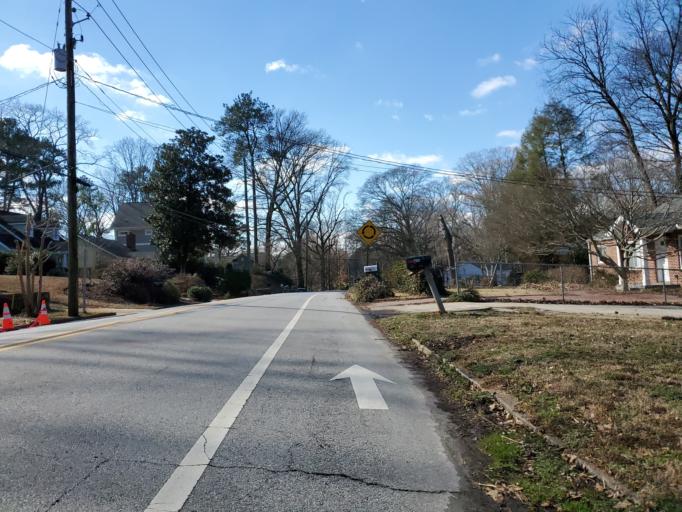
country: US
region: Georgia
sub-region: Fulton County
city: Atlanta
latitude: 33.7362
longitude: -84.3518
